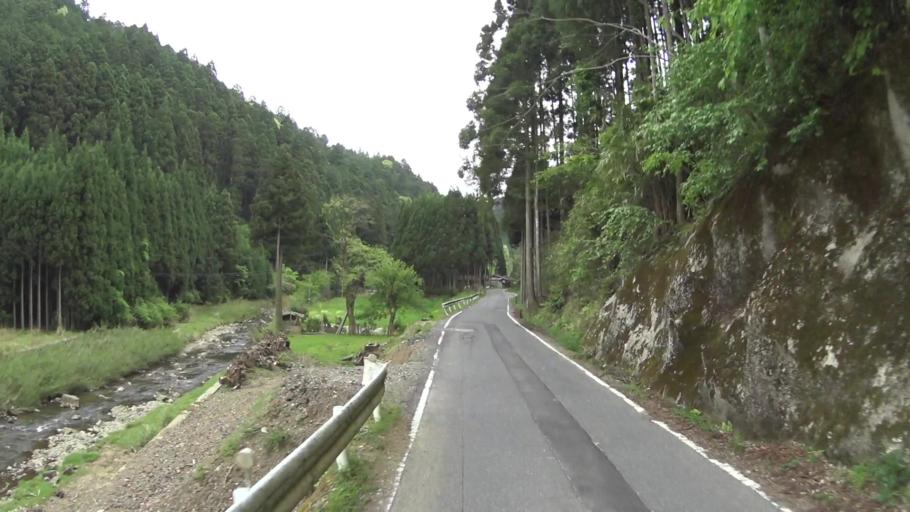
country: JP
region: Kyoto
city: Kameoka
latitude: 35.1243
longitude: 135.6223
